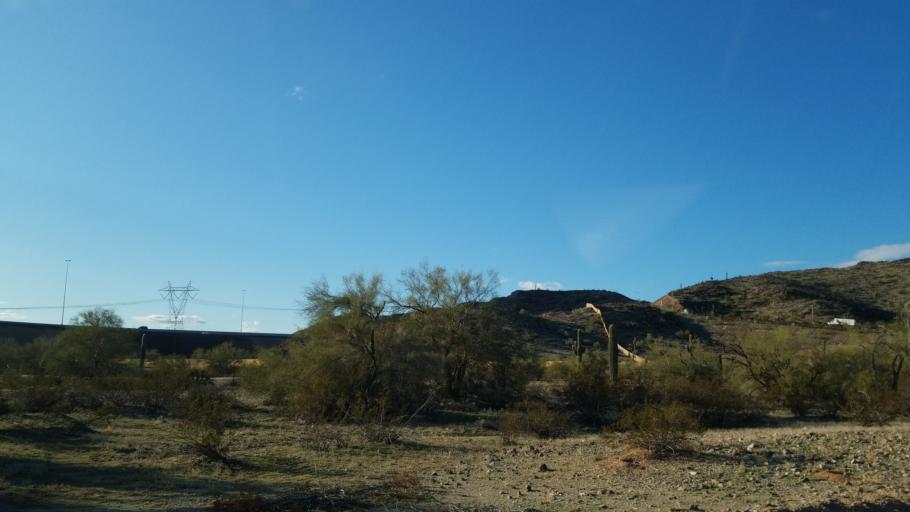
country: US
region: Arizona
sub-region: Maricopa County
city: Laveen
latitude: 33.2929
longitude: -112.1313
